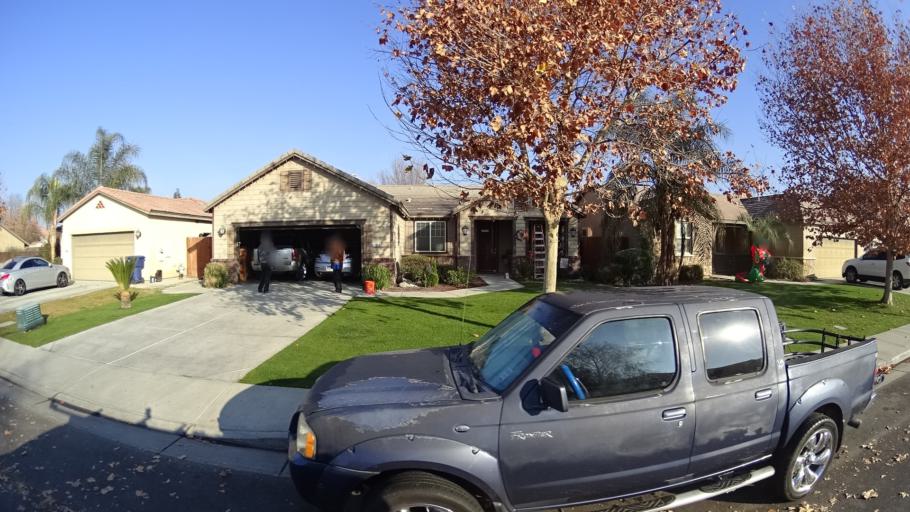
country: US
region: California
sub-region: Kern County
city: Greenacres
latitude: 35.2947
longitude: -119.1203
